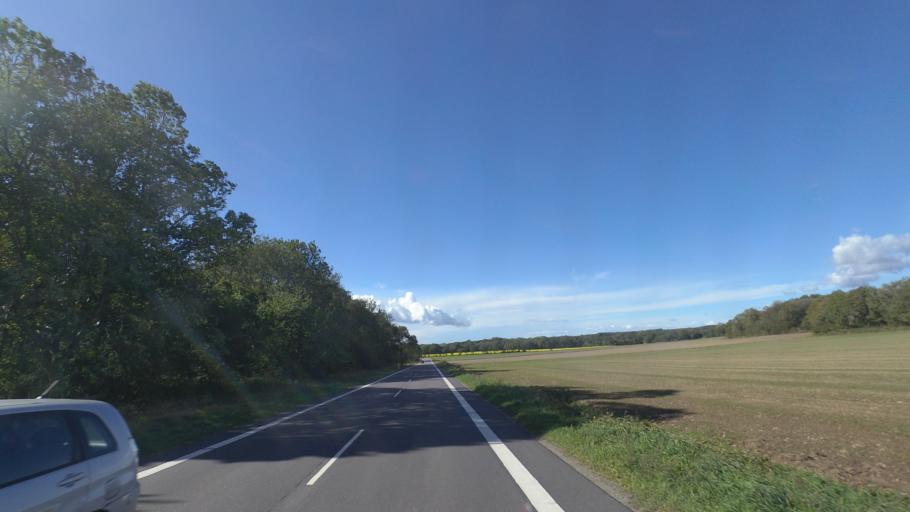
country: DK
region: Capital Region
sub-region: Bornholm Kommune
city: Akirkeby
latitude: 55.0687
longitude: 14.9903
